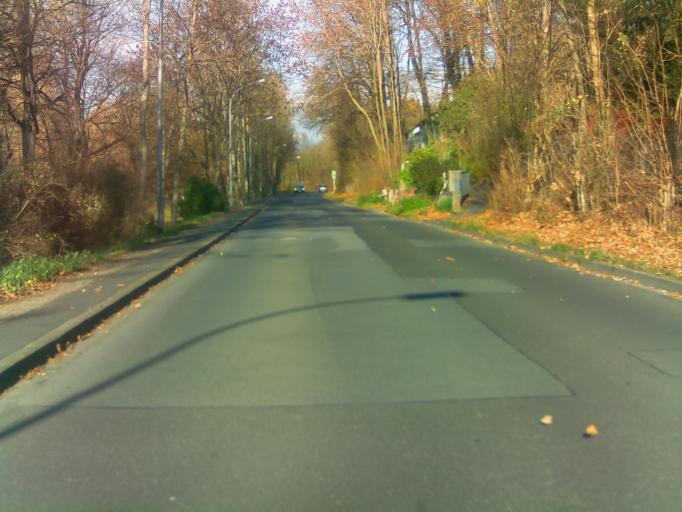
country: DE
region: Bavaria
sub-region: Regierungsbezirk Unterfranken
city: Bad Kissingen
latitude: 50.2117
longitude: 10.0726
